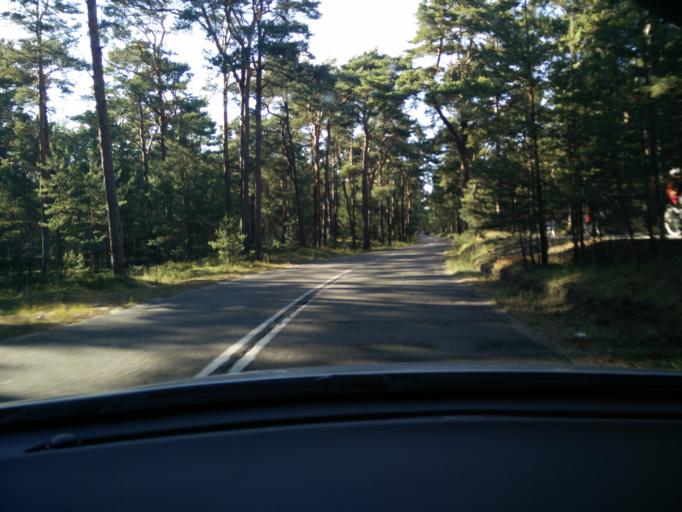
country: PL
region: Pomeranian Voivodeship
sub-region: Powiat pucki
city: Jastarnia
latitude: 54.6625
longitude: 18.7468
